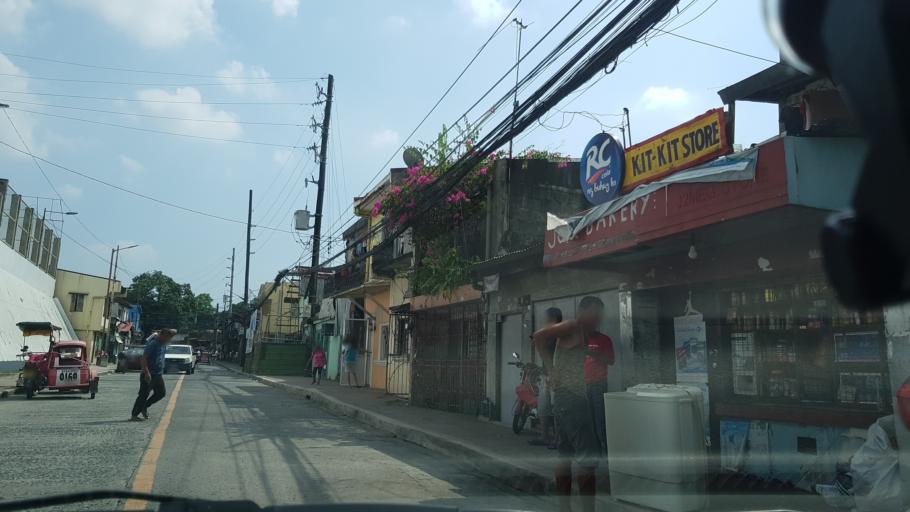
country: PH
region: Calabarzon
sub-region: Province of Rizal
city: Antipolo
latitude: 14.6604
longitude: 121.1282
